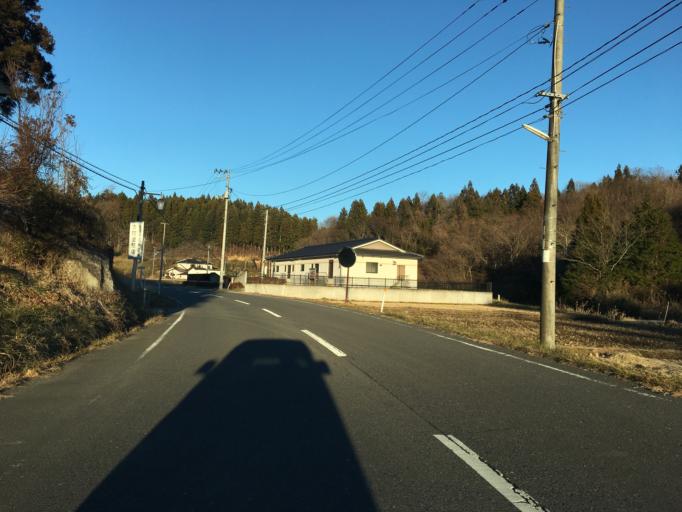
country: JP
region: Fukushima
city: Ishikawa
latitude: 37.1801
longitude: 140.5511
